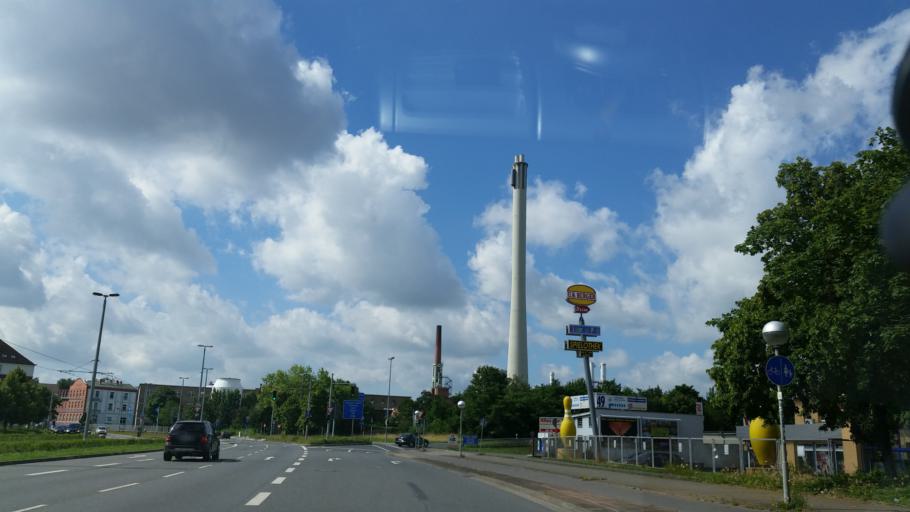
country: DE
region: Lower Saxony
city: Braunschweig
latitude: 52.2828
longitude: 10.5184
